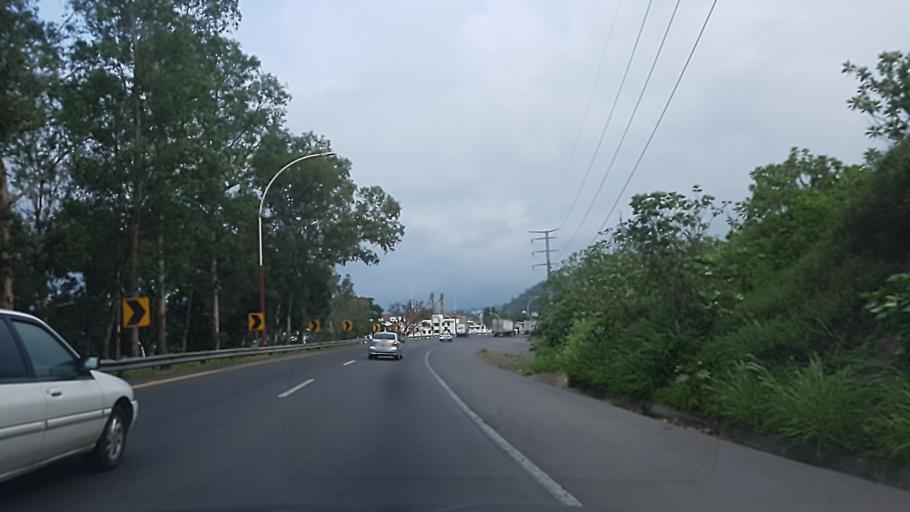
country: MX
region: Nayarit
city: Tepic
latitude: 21.4921
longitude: -104.9048
